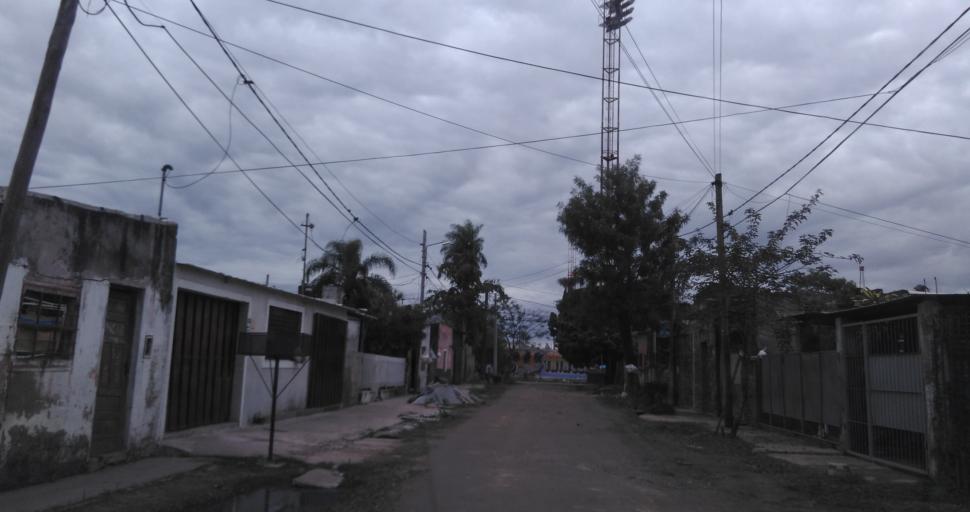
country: AR
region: Chaco
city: Resistencia
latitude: -27.4712
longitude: -58.9666
